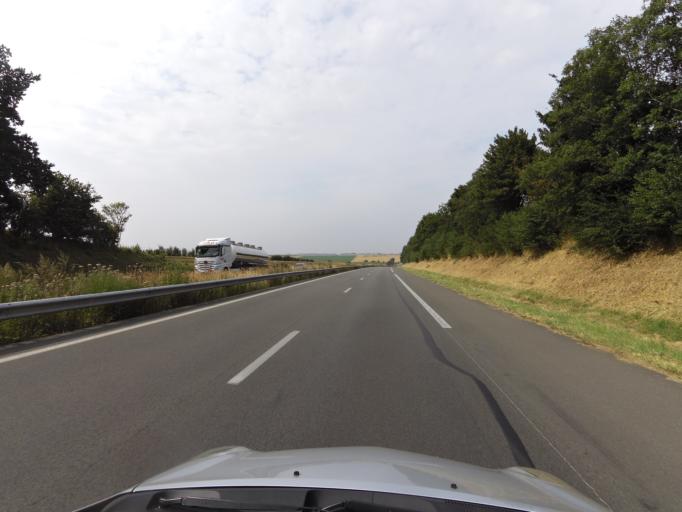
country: FR
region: Picardie
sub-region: Departement de la Somme
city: Epehy
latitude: 50.0048
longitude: 3.1766
